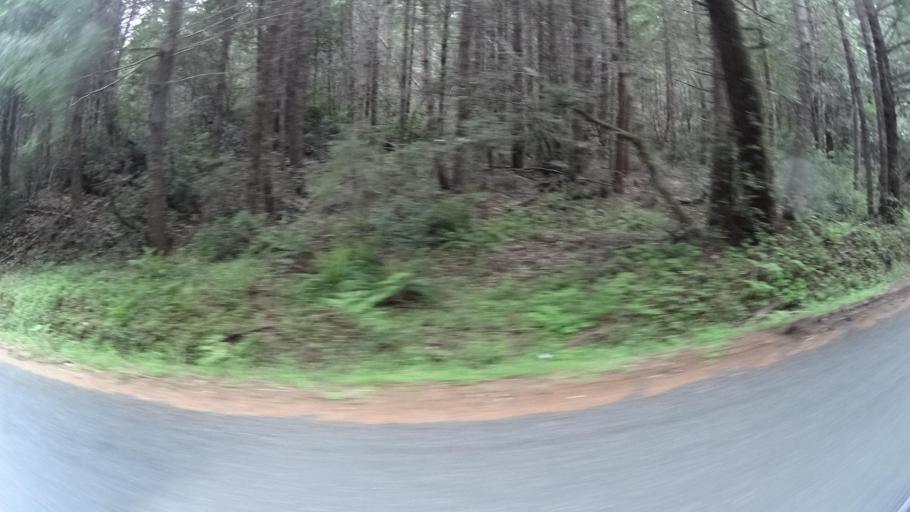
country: US
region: California
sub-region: Humboldt County
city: Willow Creek
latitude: 41.1994
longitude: -123.7631
